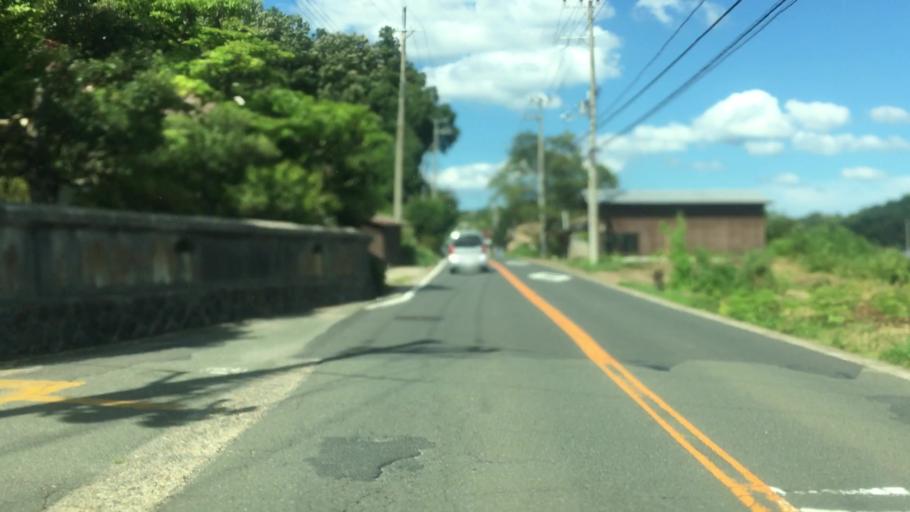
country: JP
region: Kyoto
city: Miyazu
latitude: 35.6106
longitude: 135.0533
